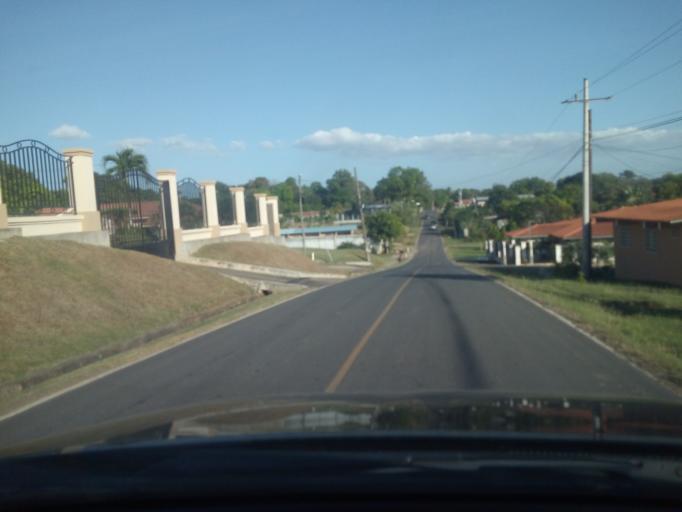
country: PA
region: Veraguas
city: Atalaya
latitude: 8.0455
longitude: -80.9306
